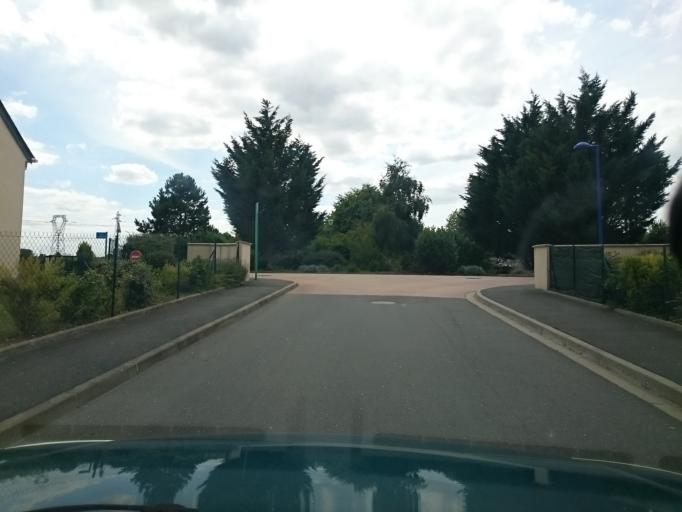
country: FR
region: Lower Normandy
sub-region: Departement du Calvados
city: Ifs
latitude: 49.1364
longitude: -0.3441
